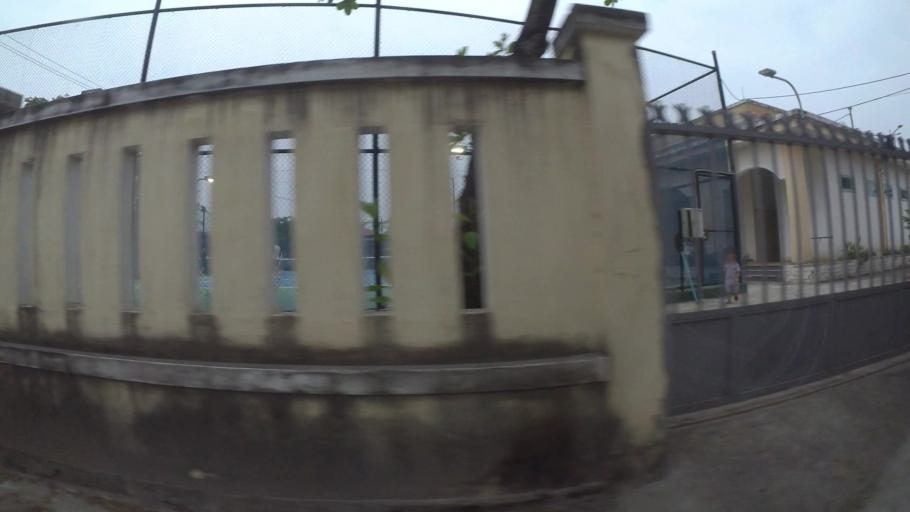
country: VN
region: Da Nang
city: Thanh Khe
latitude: 16.0480
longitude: 108.1762
